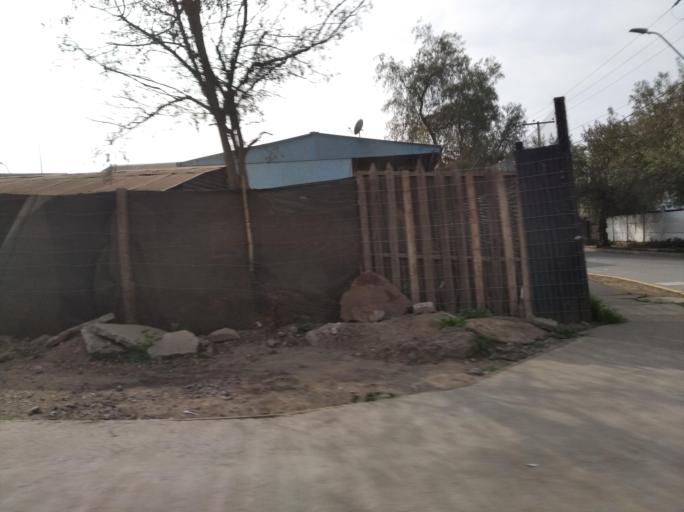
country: CL
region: Santiago Metropolitan
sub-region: Provincia de Chacabuco
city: Lampa
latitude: -33.2864
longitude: -70.8873
